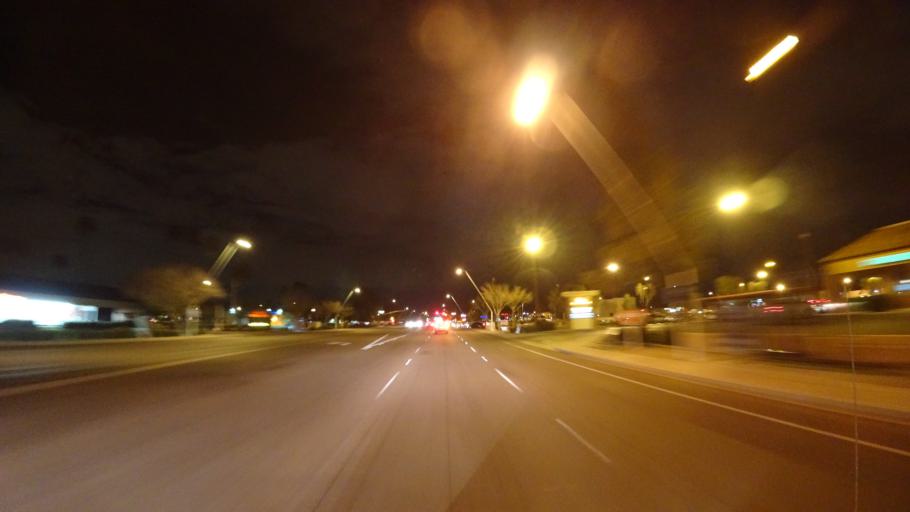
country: US
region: Arizona
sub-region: Maricopa County
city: San Carlos
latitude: 33.3481
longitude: -111.8590
